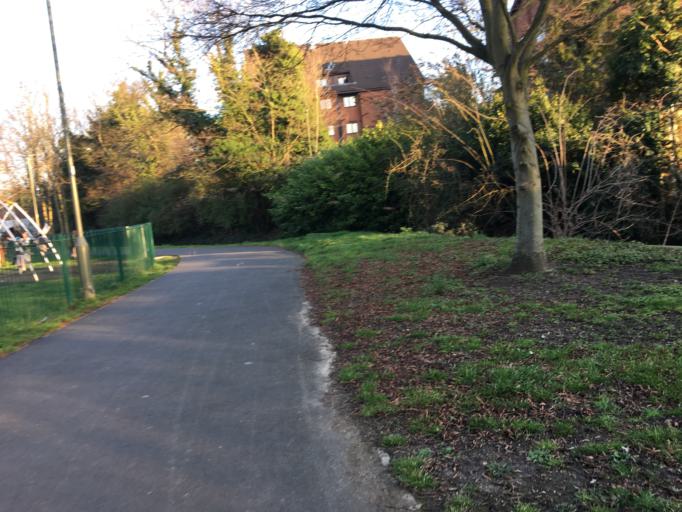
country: GB
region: England
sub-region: Greater London
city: Hendon
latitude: 51.5873
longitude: -0.2108
